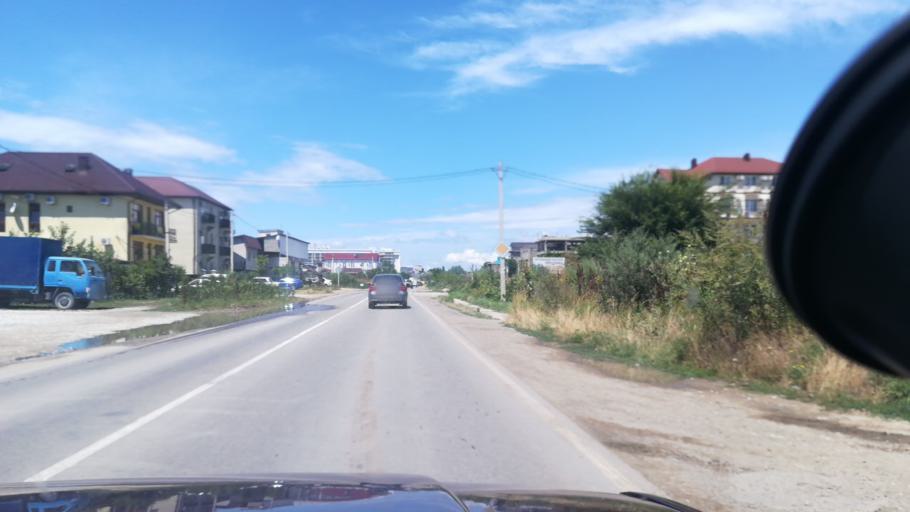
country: RU
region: Krasnodarskiy
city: Vityazevo
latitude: 44.9612
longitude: 37.2940
